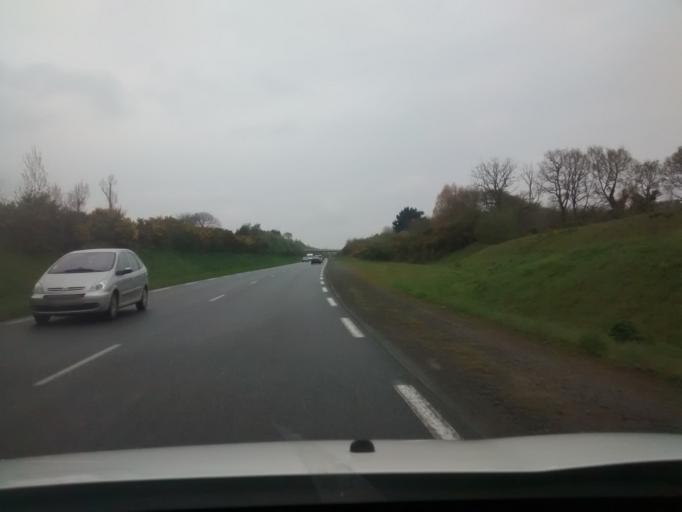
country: FR
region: Brittany
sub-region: Departement des Cotes-d'Armor
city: Lannion
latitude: 48.7447
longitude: -3.4452
